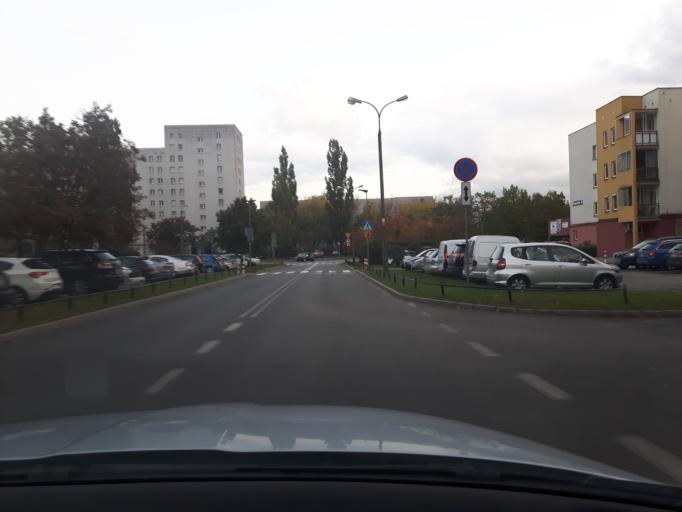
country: PL
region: Masovian Voivodeship
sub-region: Warszawa
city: Ursynow
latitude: 52.1394
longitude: 21.0525
